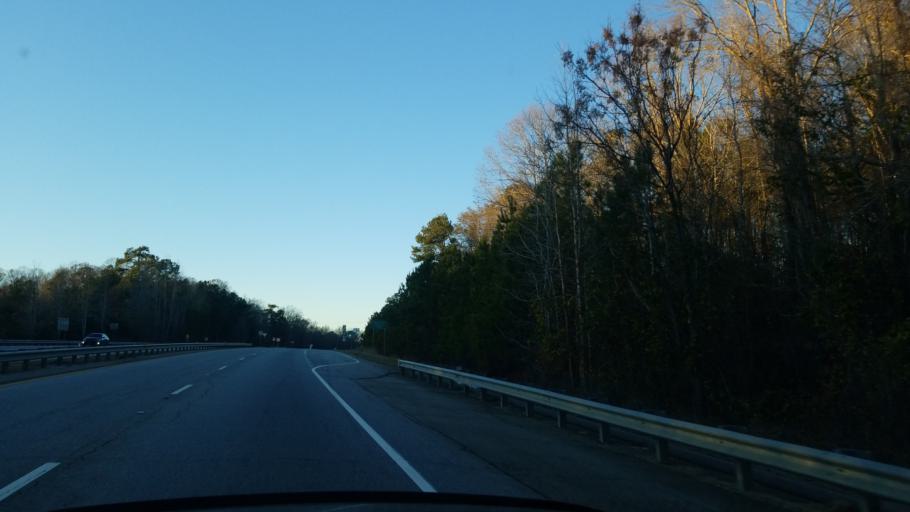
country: US
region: Georgia
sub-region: Chattahoochee County
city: Cusseta
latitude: 32.3126
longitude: -84.7977
